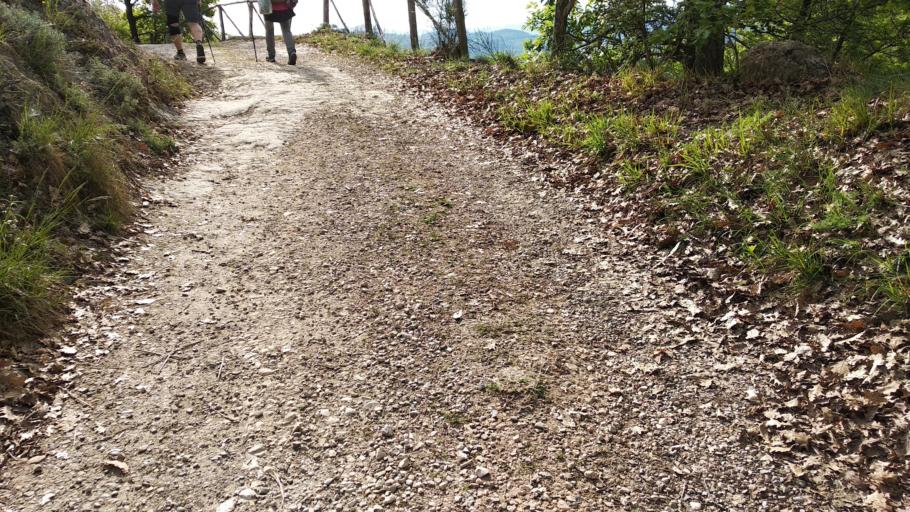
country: IT
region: Emilia-Romagna
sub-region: Provincia di Ravenna
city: Brisighella
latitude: 44.2250
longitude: 11.7563
